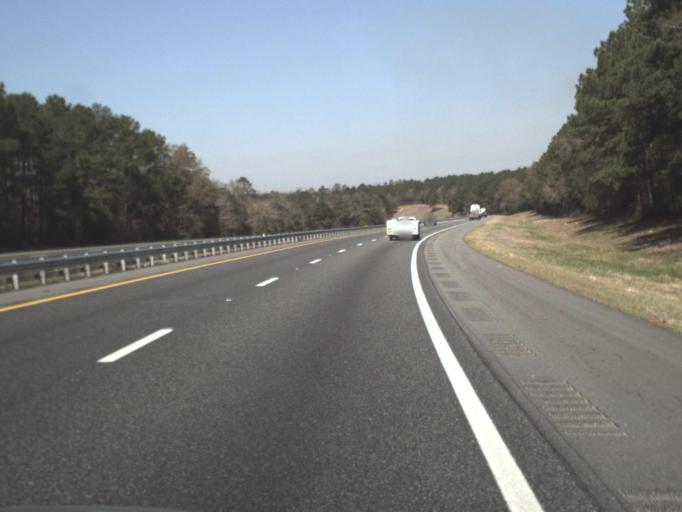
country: US
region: Florida
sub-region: Gadsden County
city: Gretna
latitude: 30.6062
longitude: -84.7401
